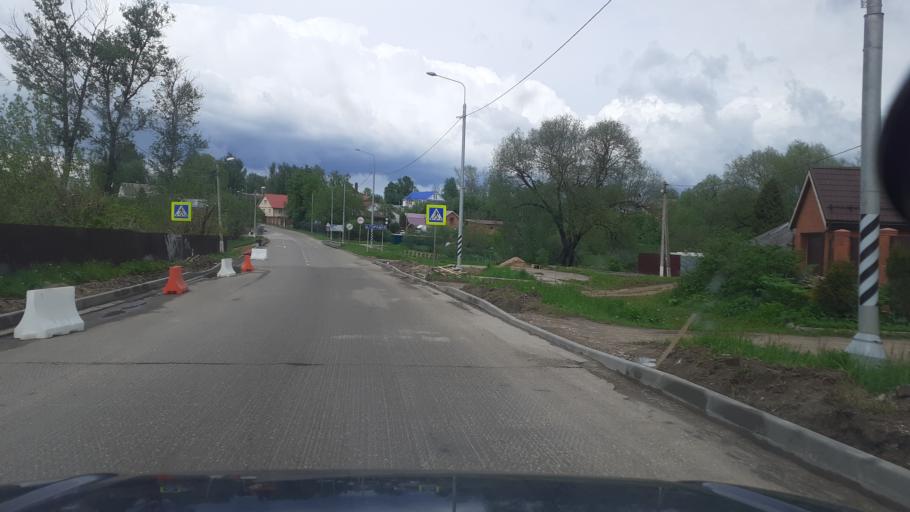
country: RU
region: Moskovskaya
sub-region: Volokolamskiy Rayon
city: Volokolamsk
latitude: 56.0400
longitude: 35.9554
